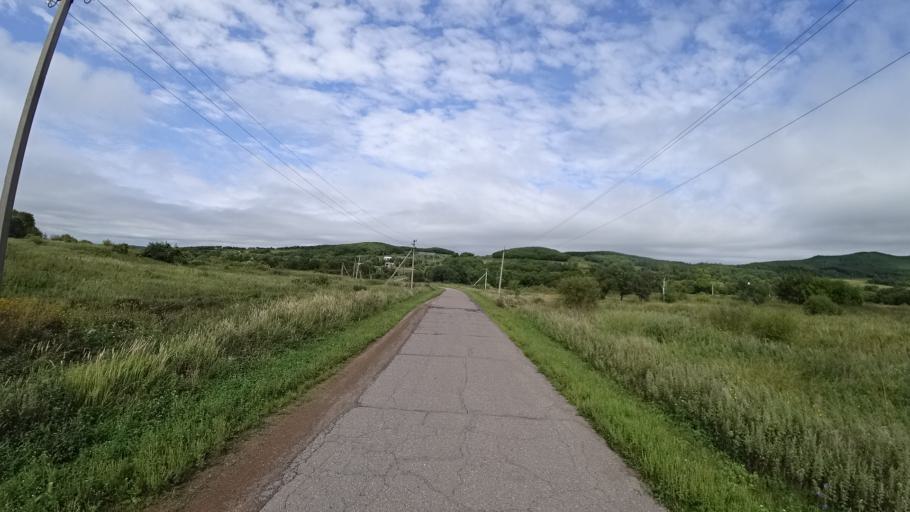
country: RU
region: Primorskiy
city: Lyalichi
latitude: 44.1336
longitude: 132.3879
